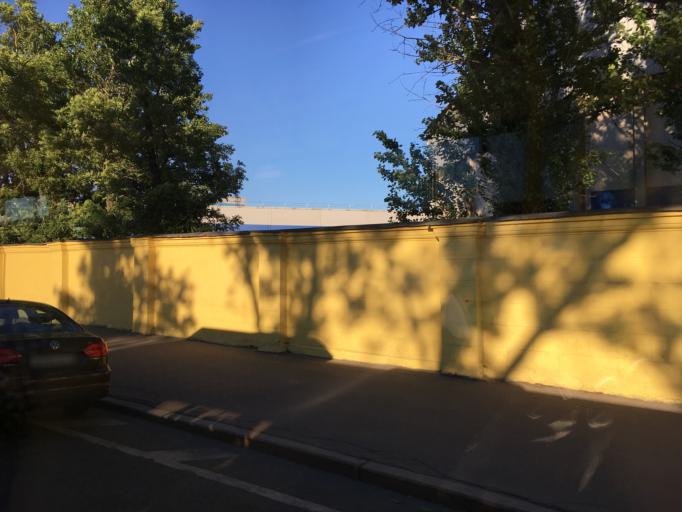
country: RU
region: St.-Petersburg
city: Centralniy
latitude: 59.8971
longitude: 30.3352
